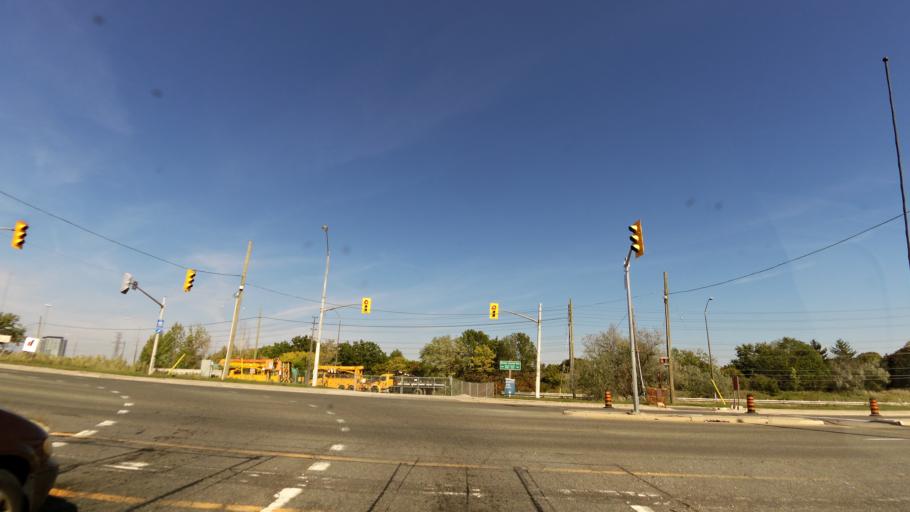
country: CA
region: Ontario
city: Mississauga
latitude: 43.5419
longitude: -79.7080
